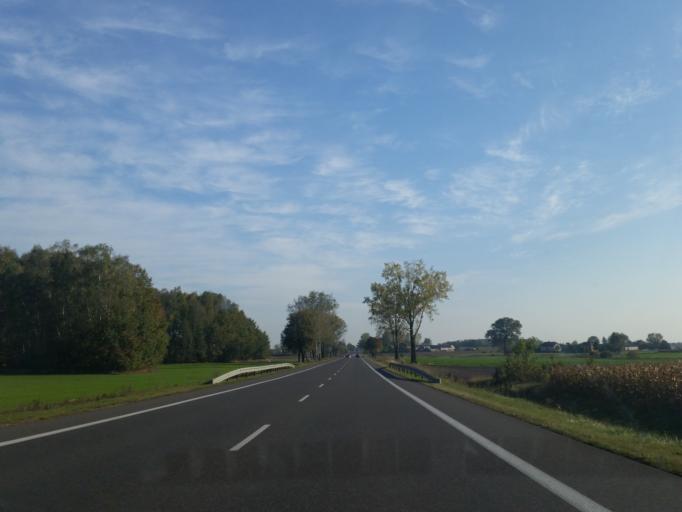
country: PL
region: Masovian Voivodeship
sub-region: Powiat plocki
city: Drobin
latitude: 52.6986
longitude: 20.0415
